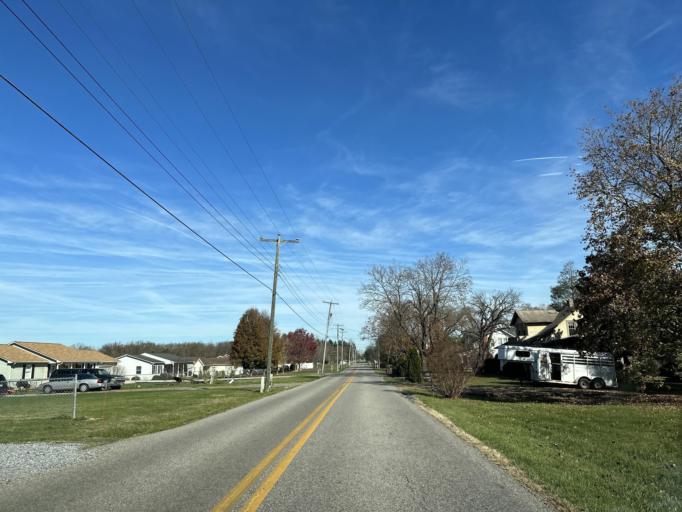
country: US
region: Virginia
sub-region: Augusta County
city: Crimora
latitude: 38.2050
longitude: -78.9038
